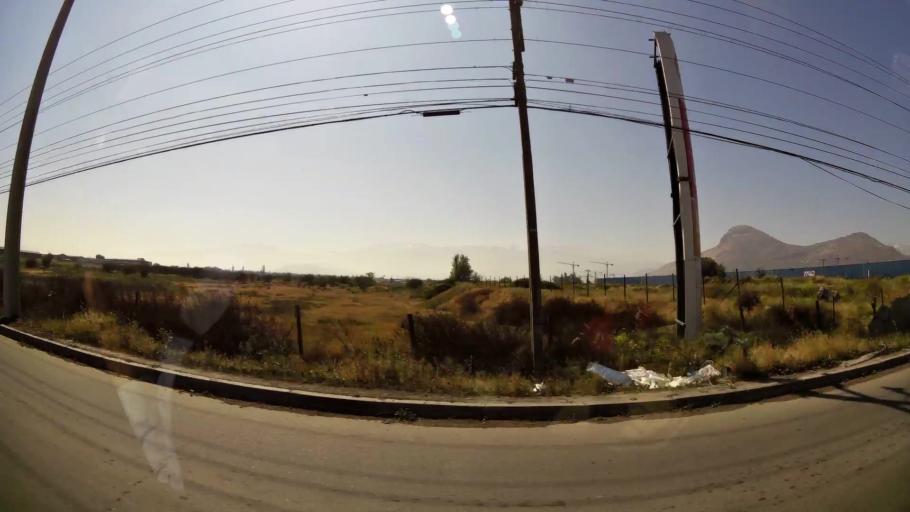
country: CL
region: Santiago Metropolitan
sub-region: Provincia de Chacabuco
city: Chicureo Abajo
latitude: -33.3065
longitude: -70.7265
